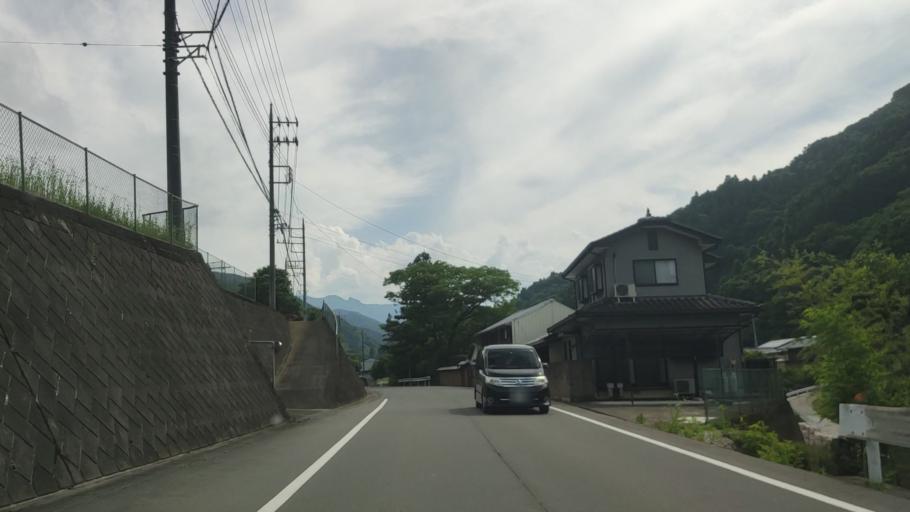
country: JP
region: Gunma
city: Tomioka
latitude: 36.1859
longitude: 138.7482
